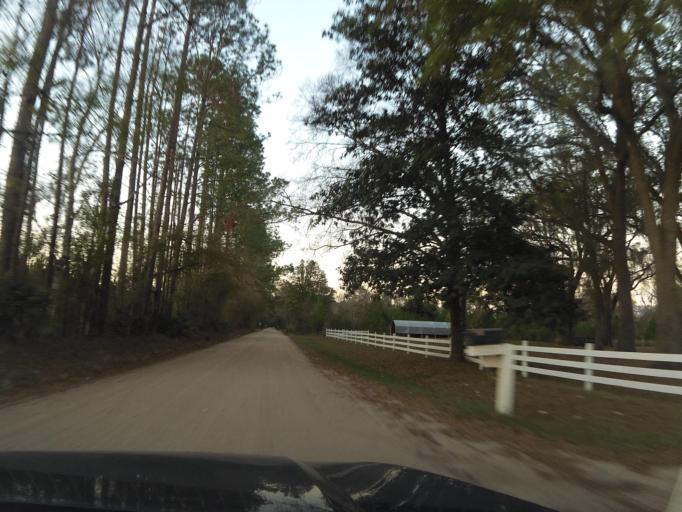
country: US
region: Florida
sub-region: Clay County
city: Asbury Lake
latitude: 29.9783
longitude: -81.7941
